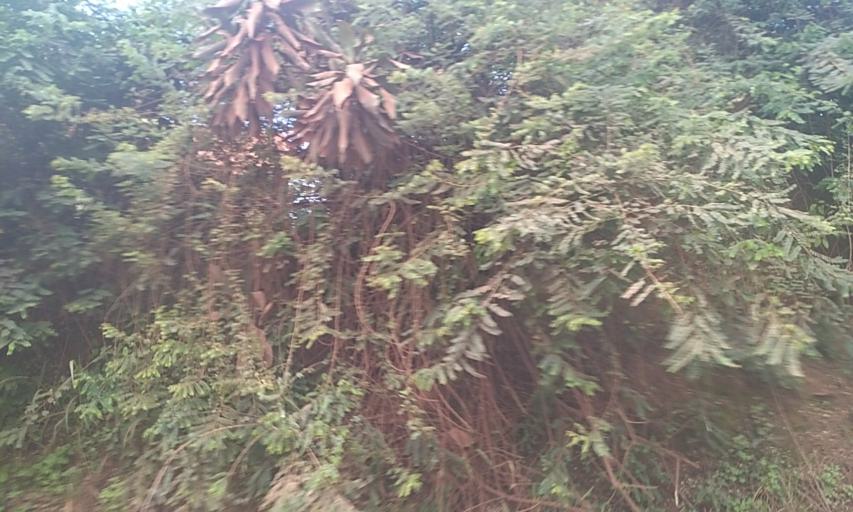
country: UG
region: Central Region
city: Kampala Central Division
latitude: 0.2838
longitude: 32.5175
